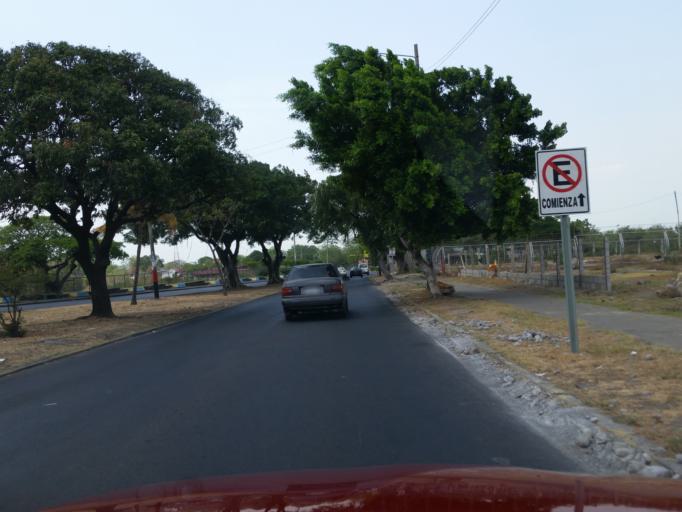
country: NI
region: Managua
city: Managua
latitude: 12.1370
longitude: -86.2685
